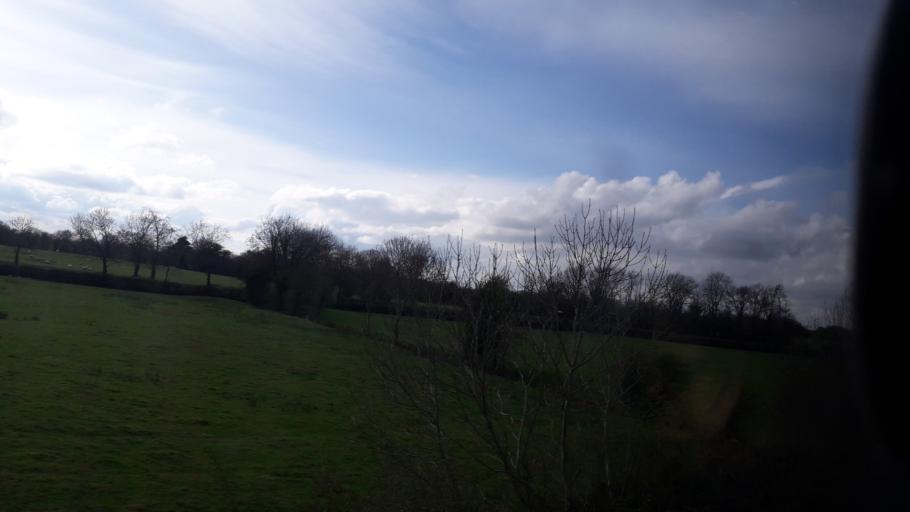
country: IE
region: Leinster
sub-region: An Mhi
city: Longwood
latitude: 53.4602
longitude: -6.9654
